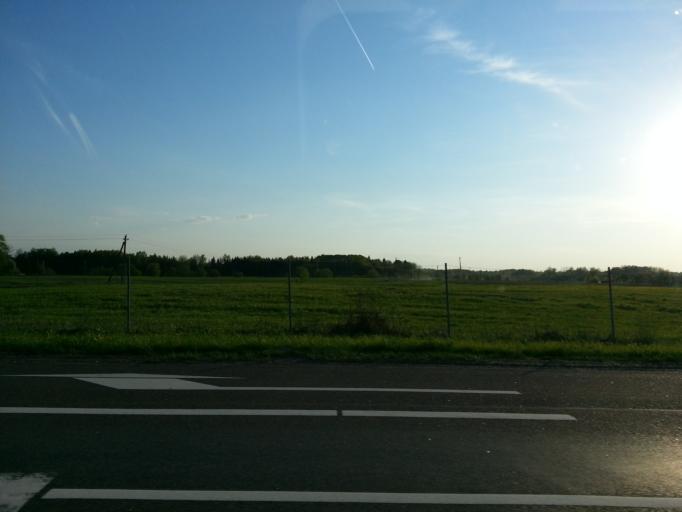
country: LT
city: Sirvintos
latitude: 55.1195
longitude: 24.8434
